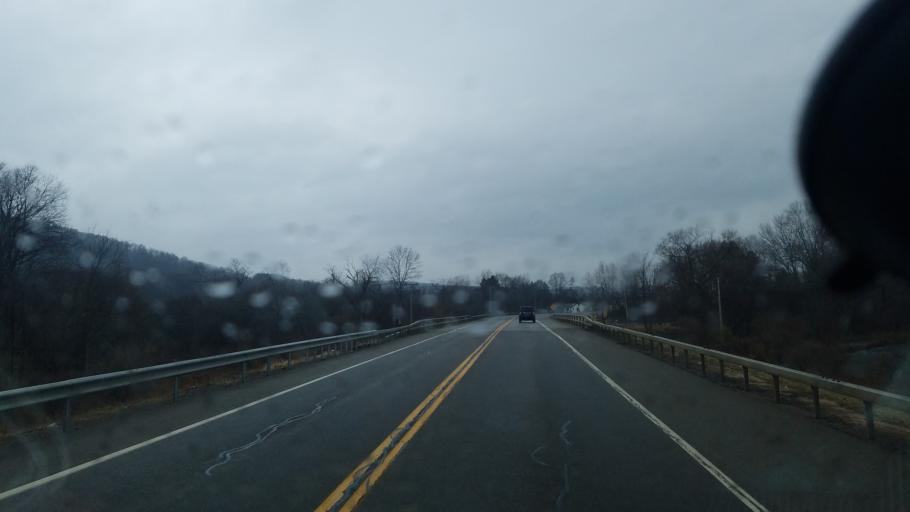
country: US
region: New York
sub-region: Allegany County
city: Wellsville
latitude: 42.0147
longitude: -77.8940
